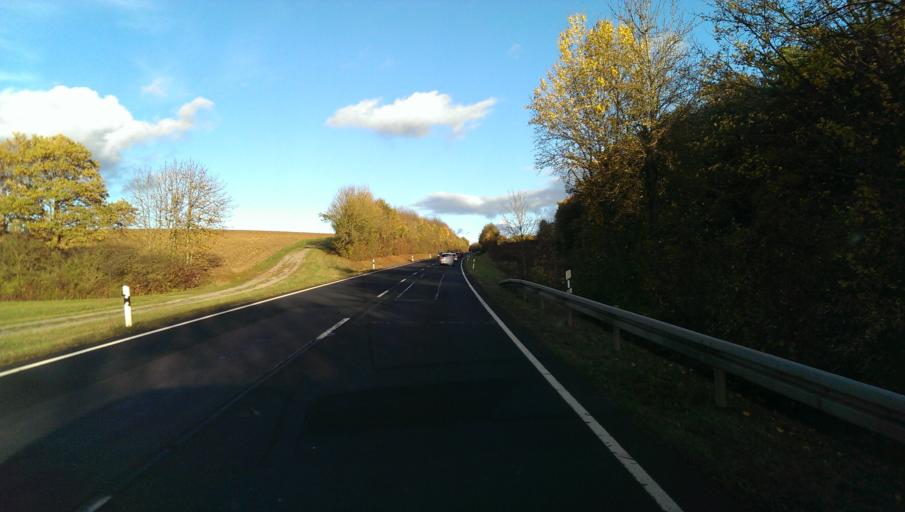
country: DE
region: Bavaria
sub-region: Regierungsbezirk Unterfranken
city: Arnstein
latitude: 49.9968
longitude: 9.9910
